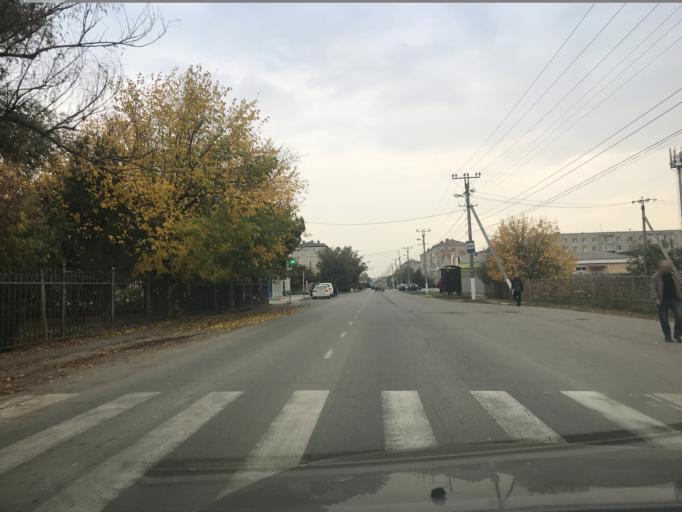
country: RU
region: Krasnodarskiy
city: Slavyansk-na-Kubani
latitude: 45.2680
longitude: 38.1069
